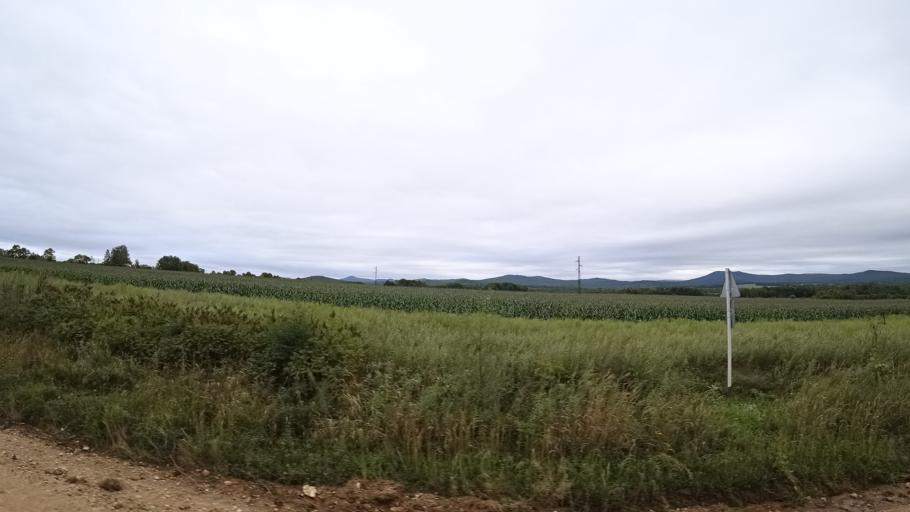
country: RU
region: Primorskiy
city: Rettikhovka
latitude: 44.1514
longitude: 132.6788
